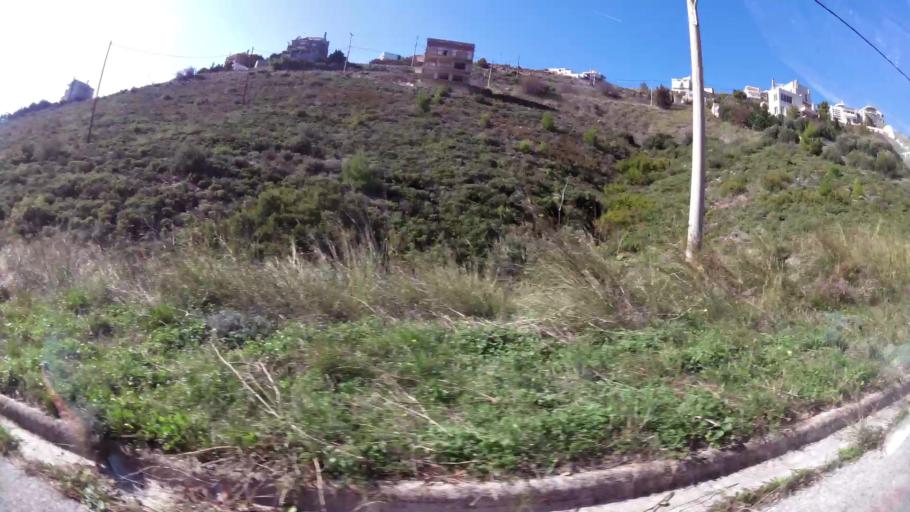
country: GR
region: Attica
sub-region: Nomarchia Anatolikis Attikis
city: Dhrafi
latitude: 38.0404
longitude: 23.8984
